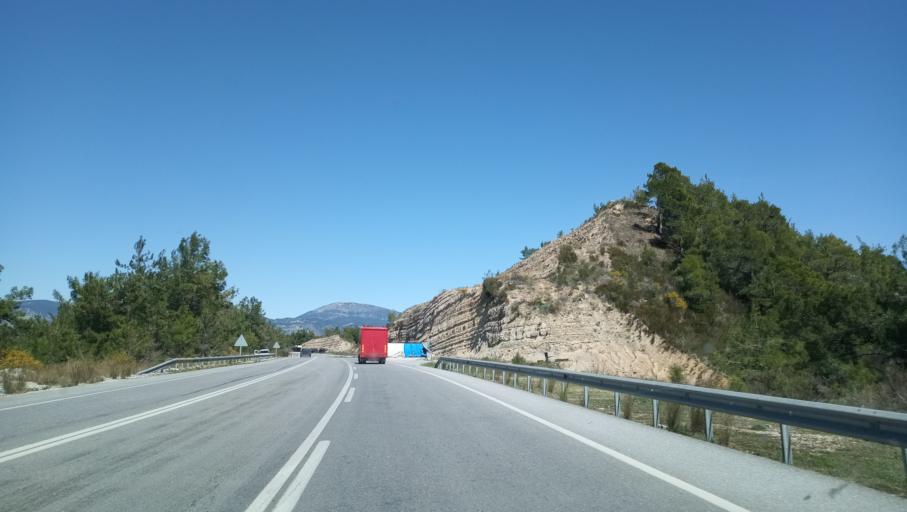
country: TR
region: Antalya
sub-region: Manavgat
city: Kizilagac
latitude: 36.7474
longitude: 31.6211
